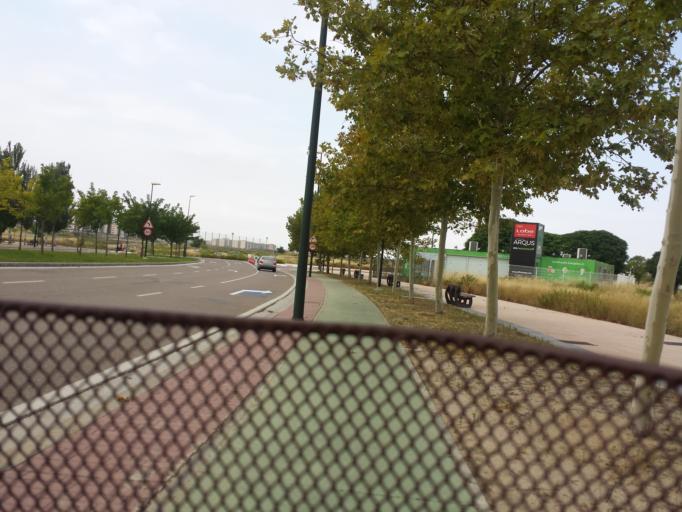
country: ES
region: Aragon
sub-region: Provincia de Zaragoza
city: Montecanal
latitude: 41.6243
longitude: -0.9399
